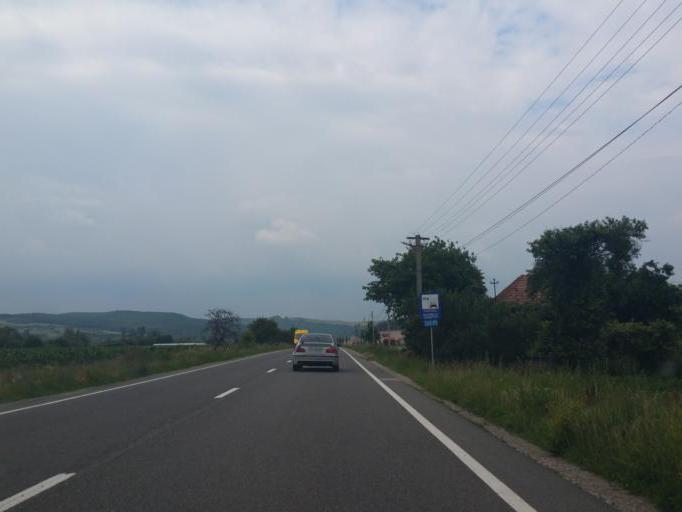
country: RO
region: Salaj
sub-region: Comuna Romanasi
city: Romanasi
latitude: 47.0964
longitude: 23.1884
